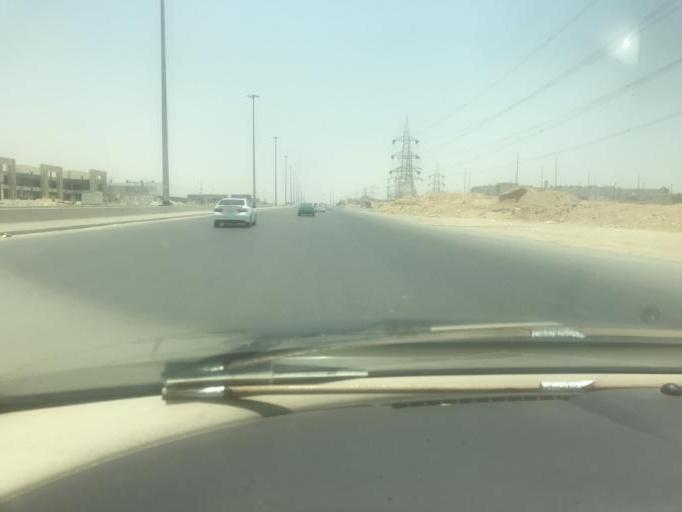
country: SA
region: Ar Riyad
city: Riyadh
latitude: 24.8146
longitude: 46.7276
